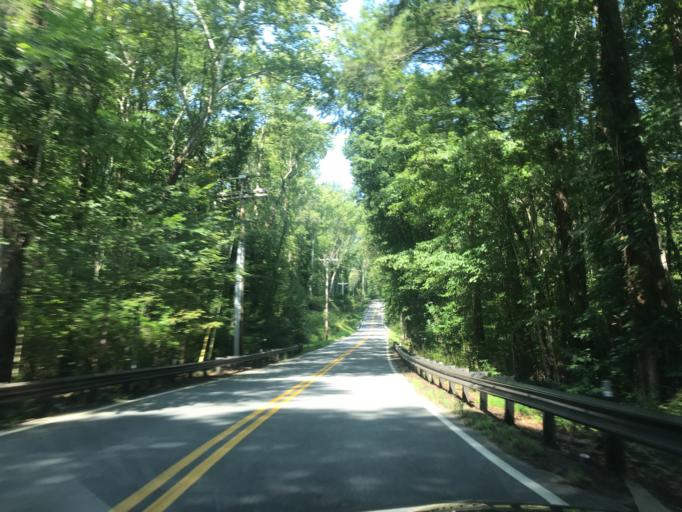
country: US
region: Maryland
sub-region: Calvert County
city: Prince Frederick
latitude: 38.4939
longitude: -76.5936
